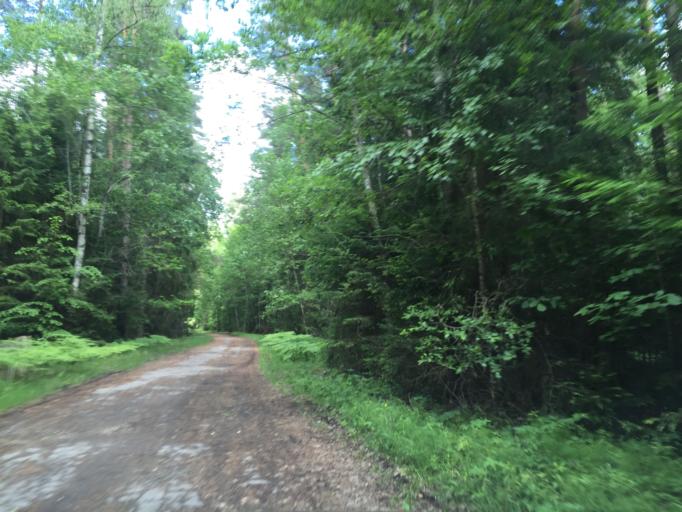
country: LV
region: Lecava
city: Iecava
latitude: 56.5494
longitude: 24.3521
